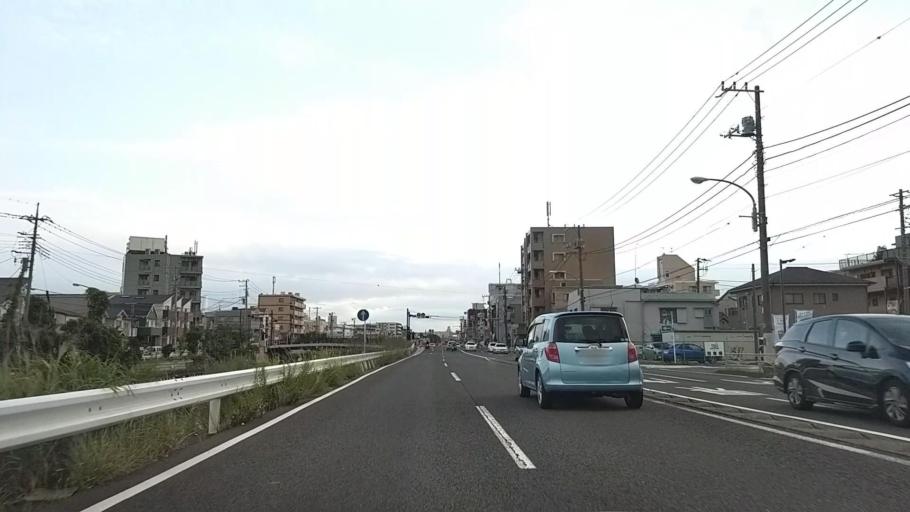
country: JP
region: Kanagawa
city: Yokohama
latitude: 35.4237
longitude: 139.6241
